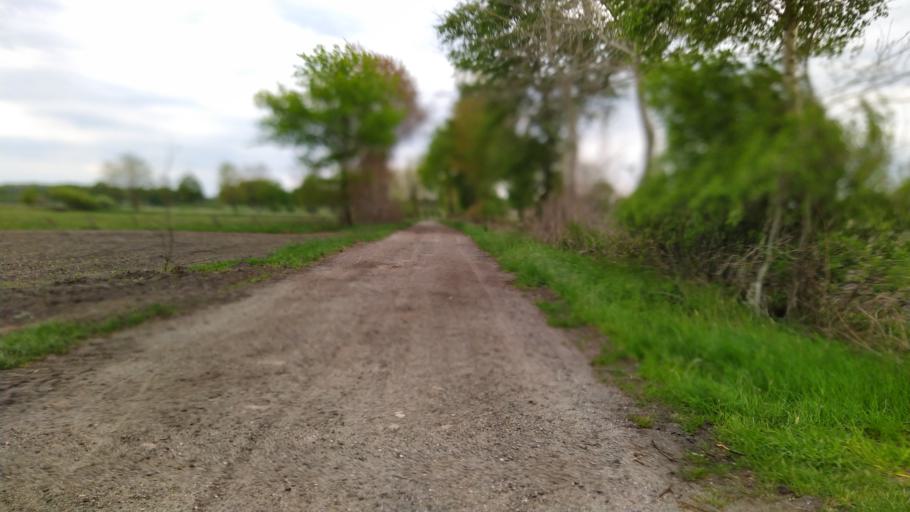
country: DE
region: Lower Saxony
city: Brest
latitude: 53.4063
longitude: 9.3983
